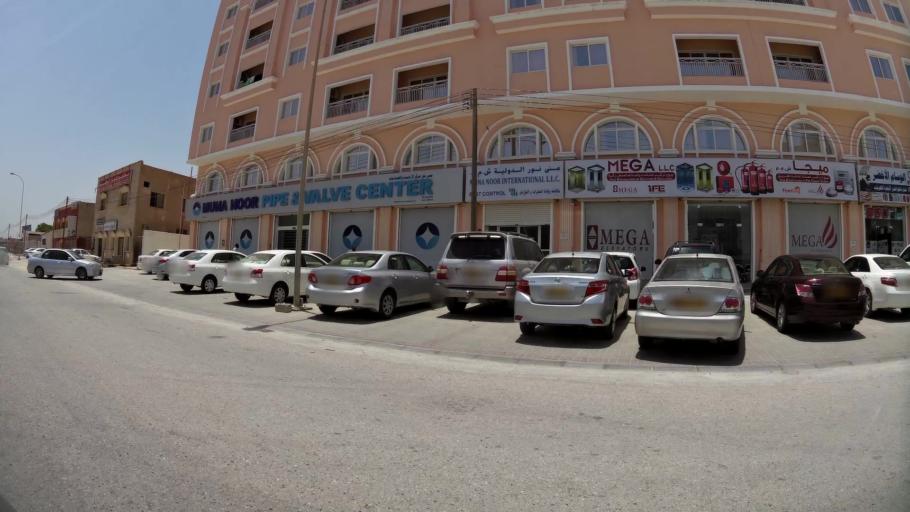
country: OM
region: Zufar
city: Salalah
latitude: 17.0212
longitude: 54.1121
